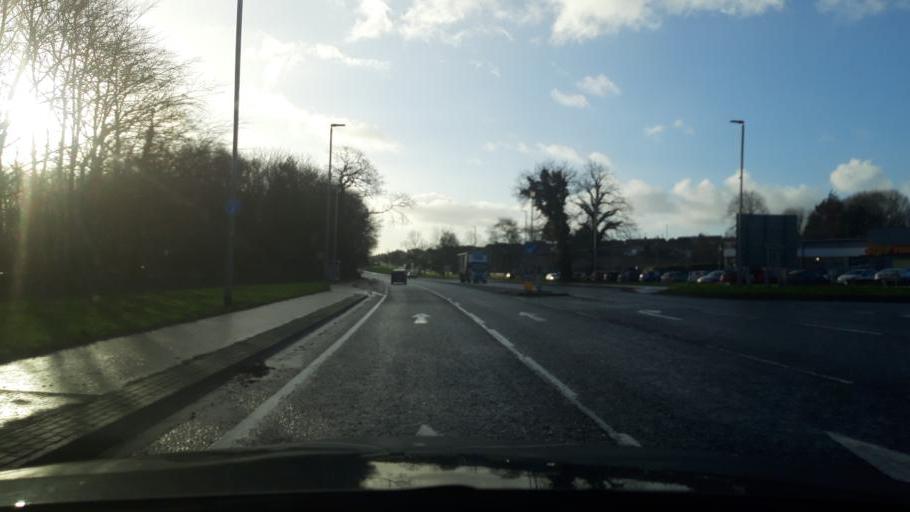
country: GB
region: Northern Ireland
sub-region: Coleraine District
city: Coleraine
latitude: 55.1196
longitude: -6.6807
